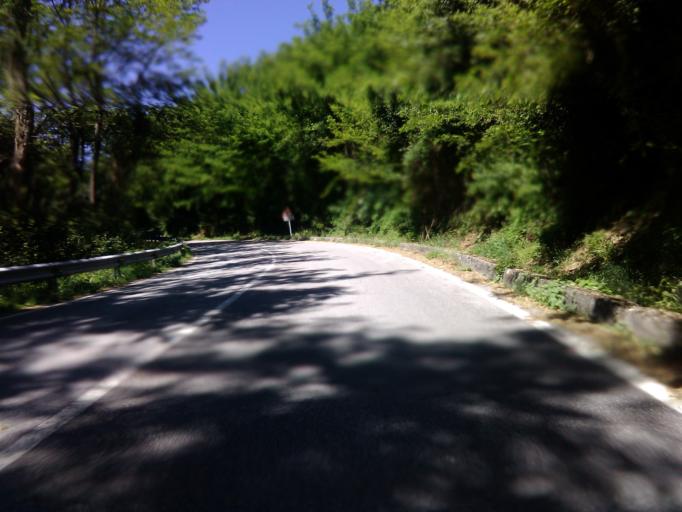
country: IT
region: Tuscany
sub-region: Provincia di Massa-Carrara
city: Pontremoli
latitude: 44.3988
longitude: 9.8831
